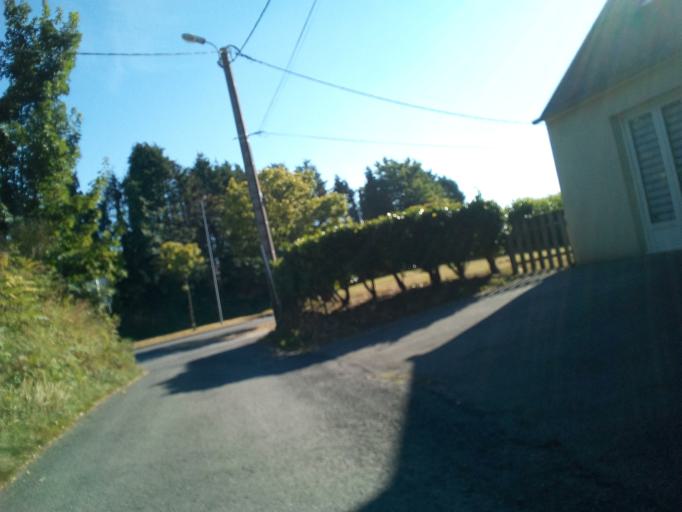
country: FR
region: Brittany
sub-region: Departement du Finistere
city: Landivisiau
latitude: 48.5050
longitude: -4.0768
